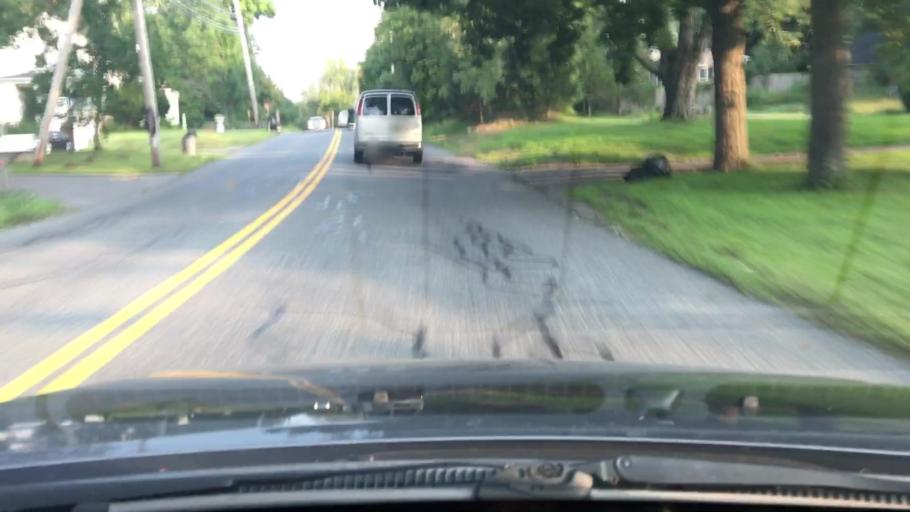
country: US
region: Massachusetts
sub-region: Worcester County
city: Milford
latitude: 42.1749
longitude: -71.5315
